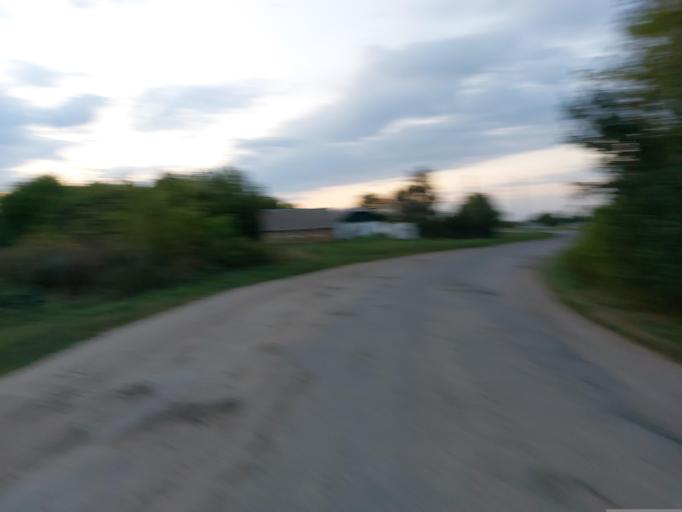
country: RU
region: Lipetsk
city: Dolgorukovo
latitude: 52.3759
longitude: 38.0515
